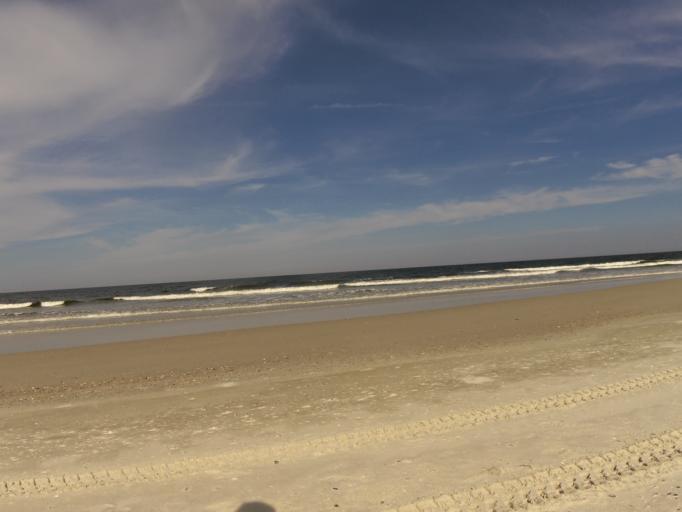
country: US
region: Florida
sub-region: Duval County
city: Atlantic Beach
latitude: 30.4506
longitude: -81.4101
